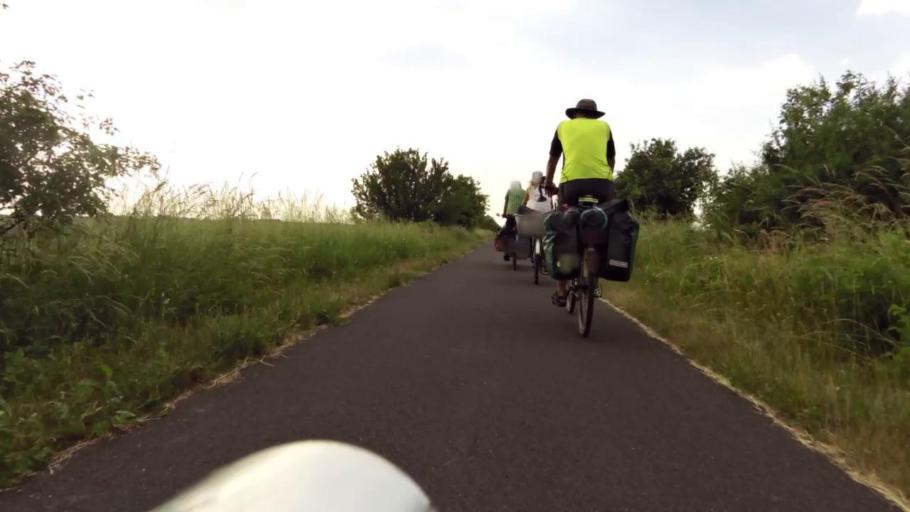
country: PL
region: Kujawsko-Pomorskie
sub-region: Powiat torunski
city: Lubianka
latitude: 53.1161
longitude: 18.4707
